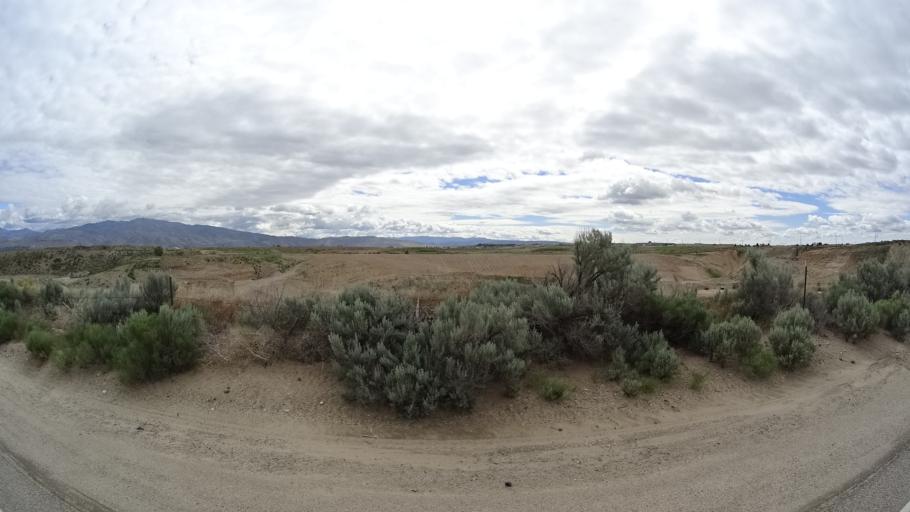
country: US
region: Idaho
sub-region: Ada County
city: Boise
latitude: 43.5518
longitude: -116.1877
